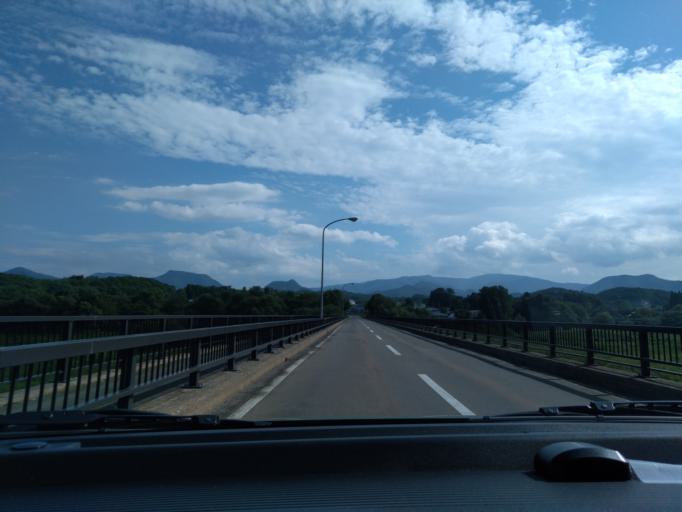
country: JP
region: Iwate
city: Shizukuishi
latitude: 39.6674
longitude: 140.9818
